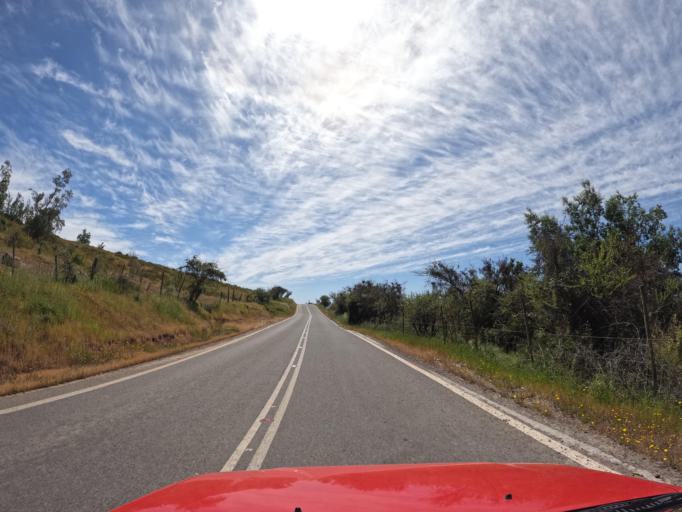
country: CL
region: Maule
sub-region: Provincia de Talca
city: Talca
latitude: -35.0623
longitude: -71.7356
